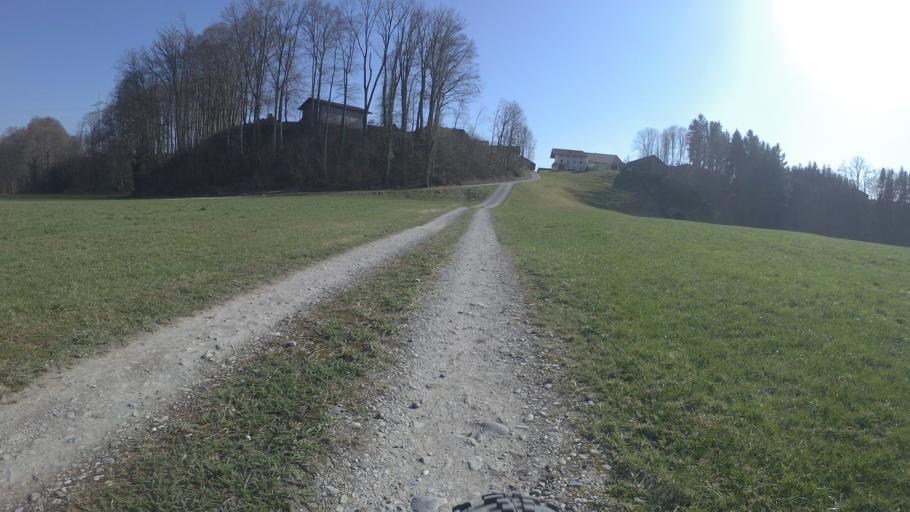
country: DE
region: Bavaria
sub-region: Upper Bavaria
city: Nussdorf
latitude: 47.9240
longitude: 12.6162
